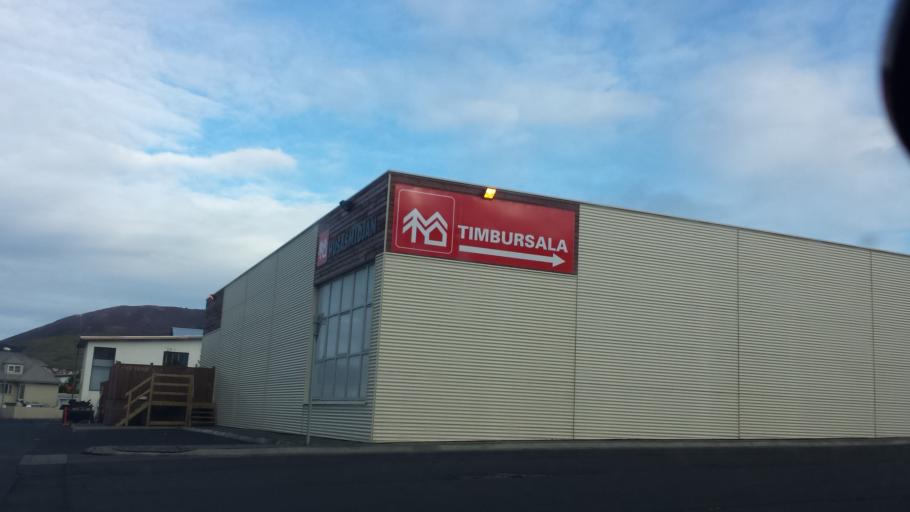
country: IS
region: South
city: Vestmannaeyjar
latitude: 63.4419
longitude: -20.2765
